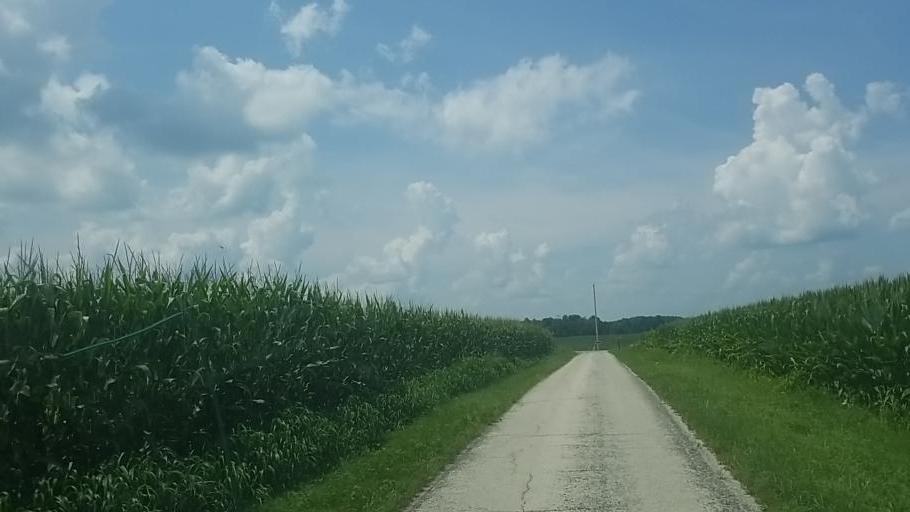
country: US
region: Ohio
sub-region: Crawford County
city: Bucyrus
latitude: 40.7460
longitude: -83.1105
